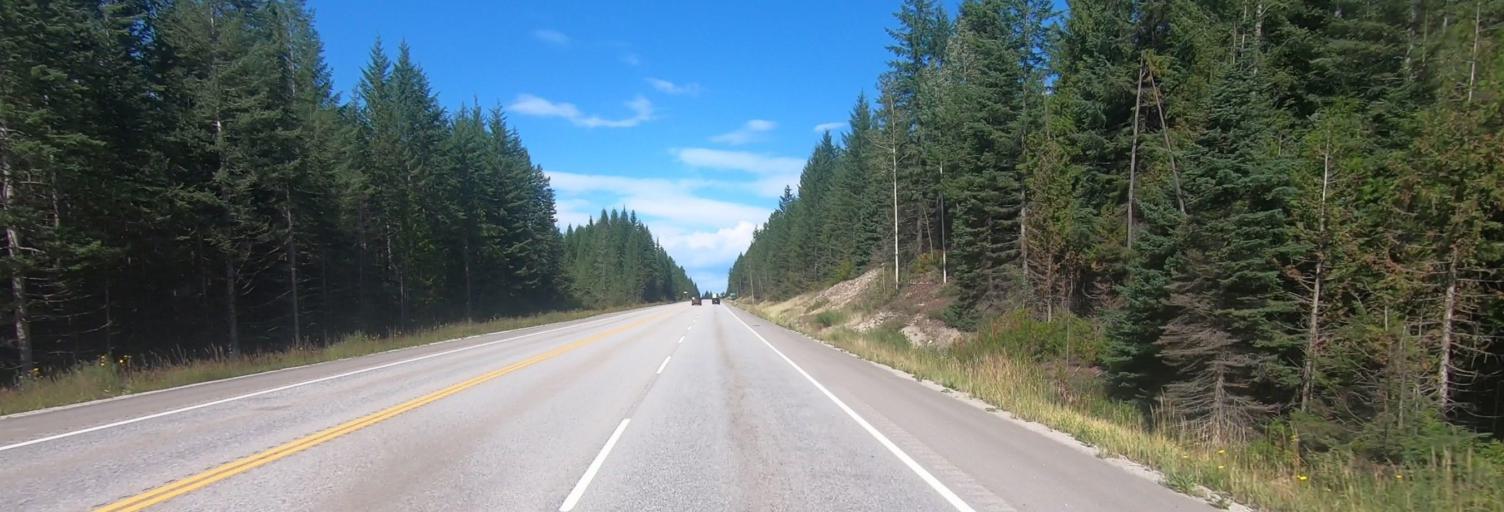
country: CA
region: British Columbia
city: Golden
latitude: 51.4811
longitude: -117.2438
